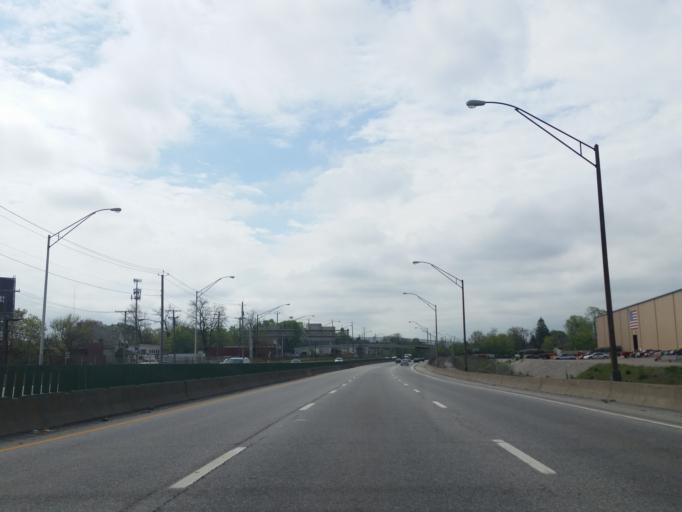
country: US
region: Ohio
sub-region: Cuyahoga County
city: Newburgh Heights
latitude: 41.4629
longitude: -81.6575
